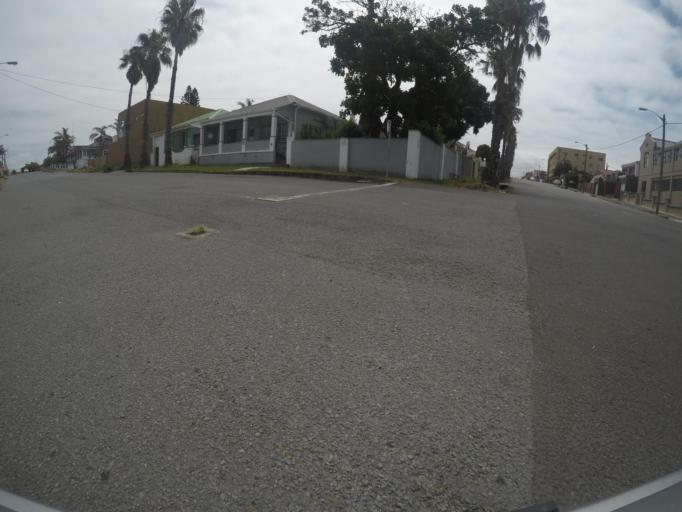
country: ZA
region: Eastern Cape
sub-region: Buffalo City Metropolitan Municipality
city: East London
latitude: -33.0204
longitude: 27.9161
